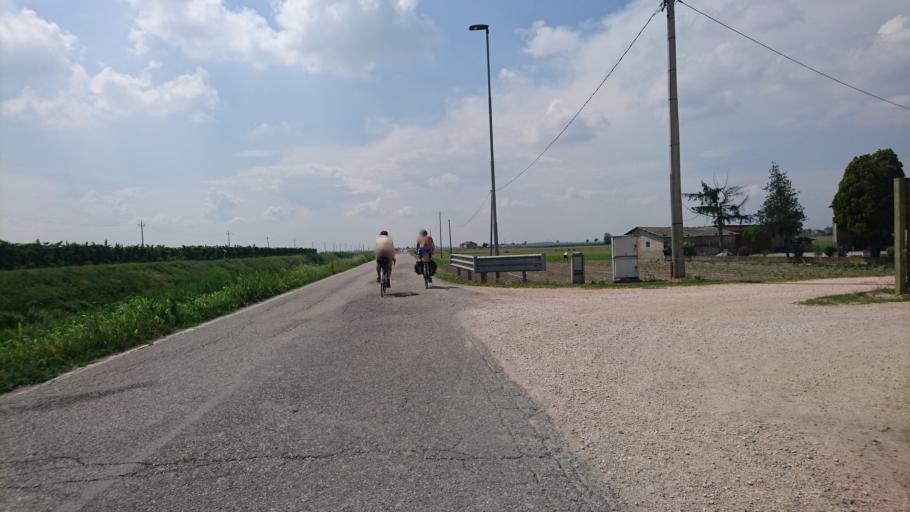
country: IT
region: Veneto
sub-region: Provincia di Rovigo
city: Giacciano con Baruchella
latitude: 45.0706
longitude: 11.4178
